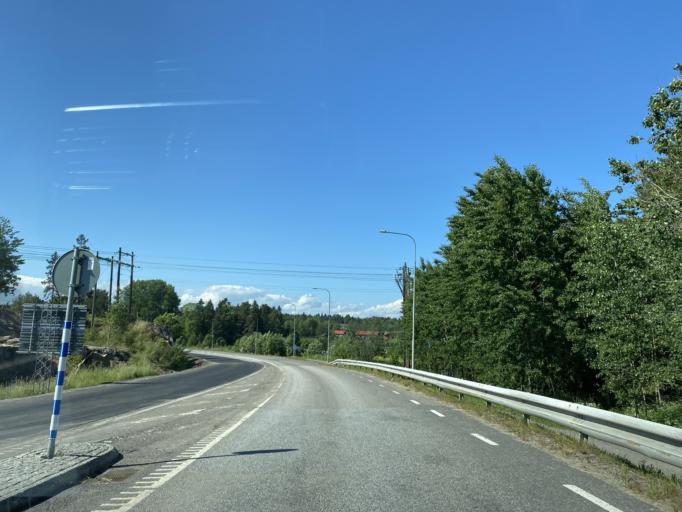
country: SE
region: Stockholm
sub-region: Norrtalje Kommun
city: Norrtalje
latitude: 59.7668
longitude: 18.6918
